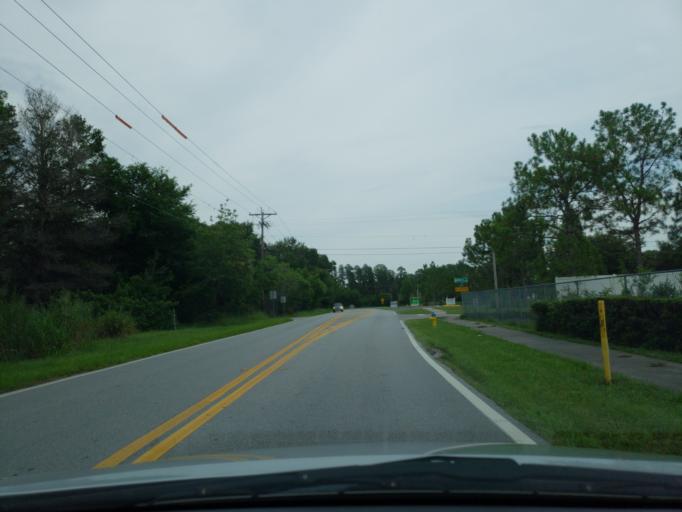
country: US
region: Florida
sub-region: Hillsborough County
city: Lutz
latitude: 28.1578
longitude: -82.4811
